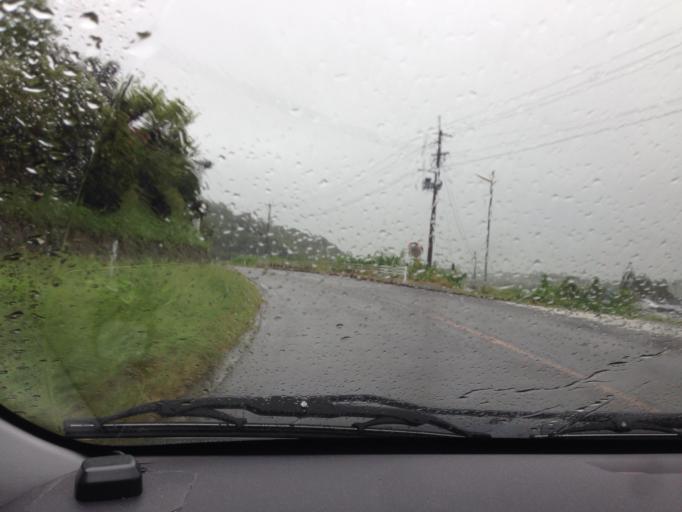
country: JP
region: Fukushima
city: Koriyama
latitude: 37.4157
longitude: 140.2815
